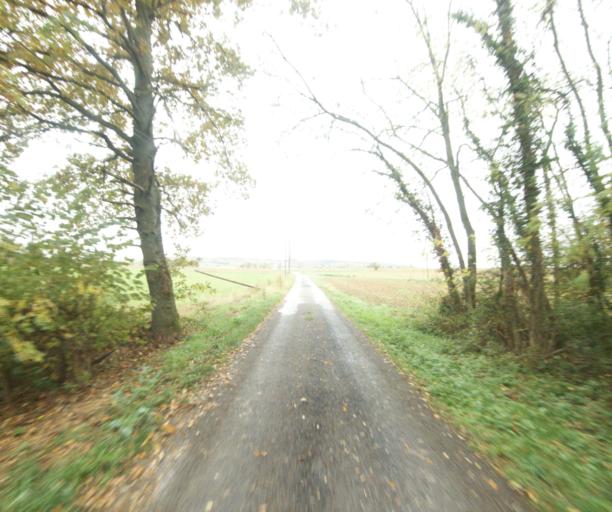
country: FR
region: Rhone-Alpes
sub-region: Departement de l'Ain
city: Pont-de-Vaux
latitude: 46.4847
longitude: 4.8794
